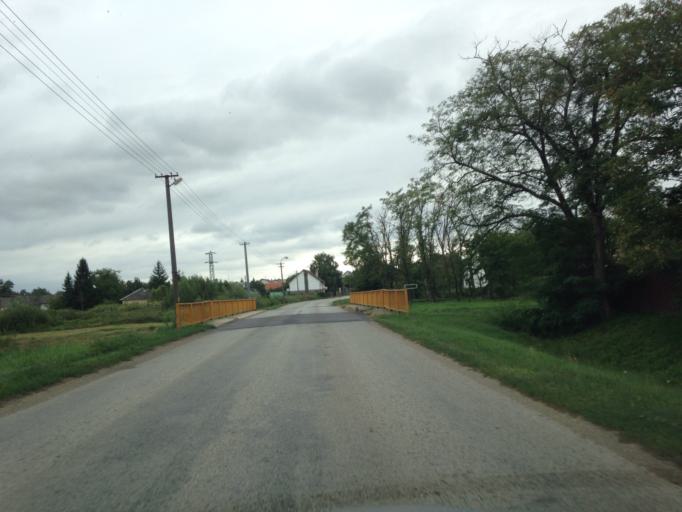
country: SK
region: Nitriansky
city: Svodin
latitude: 47.8989
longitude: 18.4204
